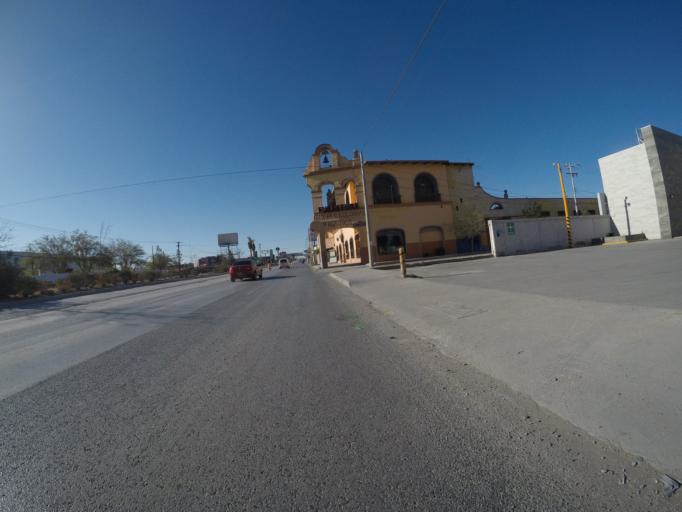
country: MX
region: Chihuahua
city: Ciudad Juarez
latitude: 31.6812
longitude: -106.4248
